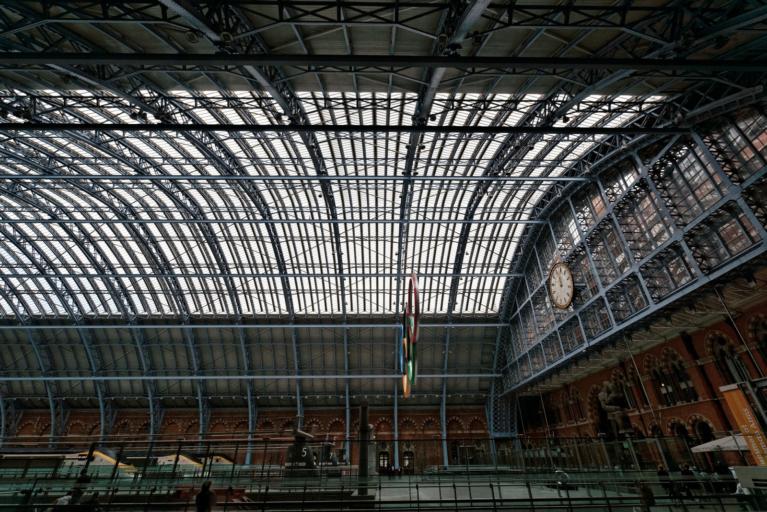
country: GB
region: England
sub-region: Greater London
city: Barnsbury
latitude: 51.5302
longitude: -0.1257
